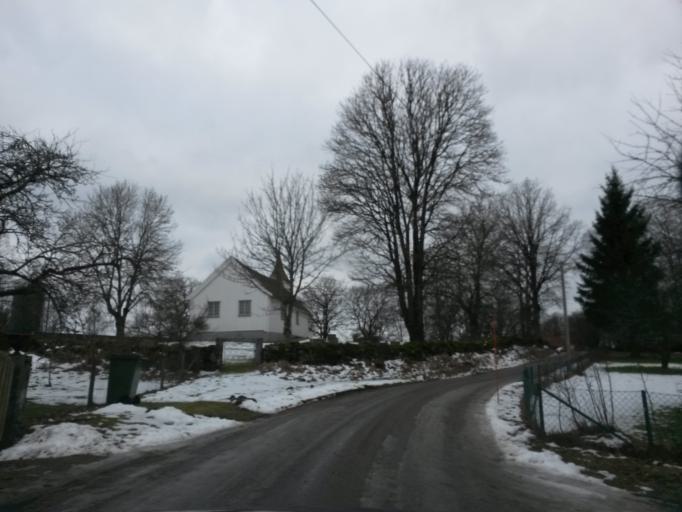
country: SE
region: Vaestra Goetaland
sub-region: Vargarda Kommun
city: Vargarda
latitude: 58.0317
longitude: 12.8882
